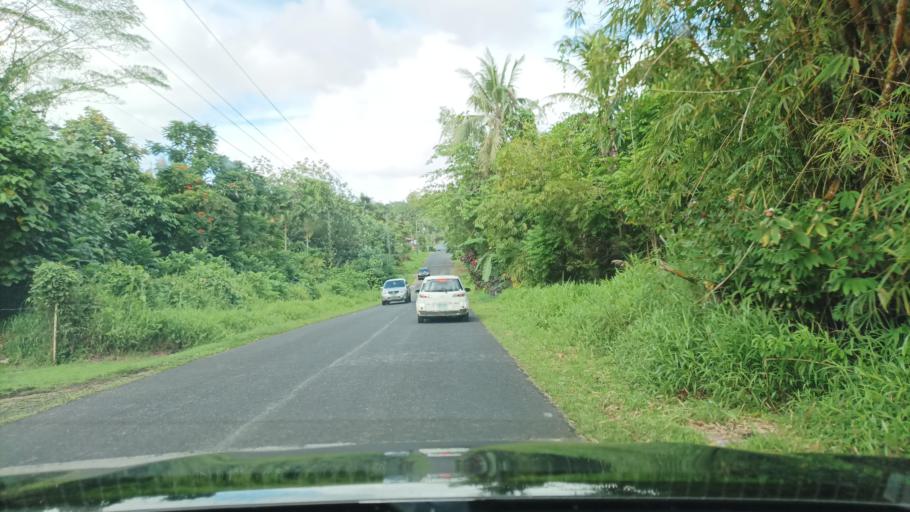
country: FM
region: Pohnpei
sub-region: Sokehs Municipality
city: Palikir - National Government Center
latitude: 6.9208
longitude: 158.1642
